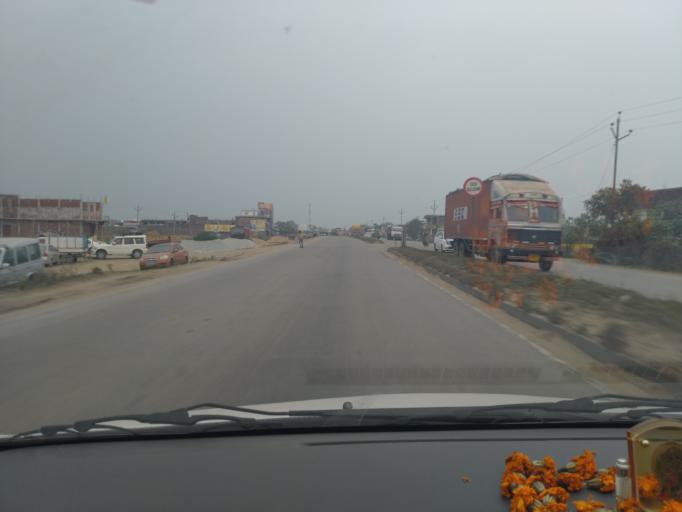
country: IN
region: Bihar
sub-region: Rohtas
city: Dehri
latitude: 24.9741
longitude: 83.9056
